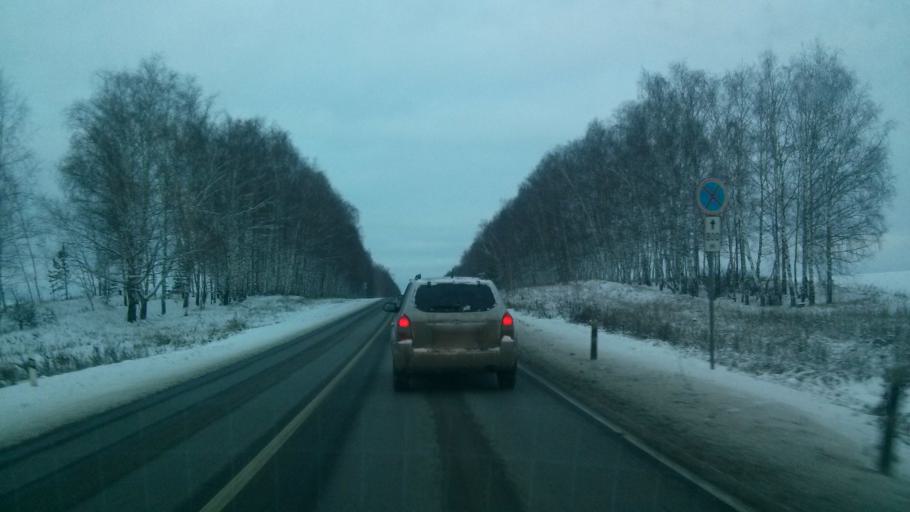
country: RU
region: Nizjnij Novgorod
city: Vorsma
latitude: 56.0252
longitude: 43.3563
